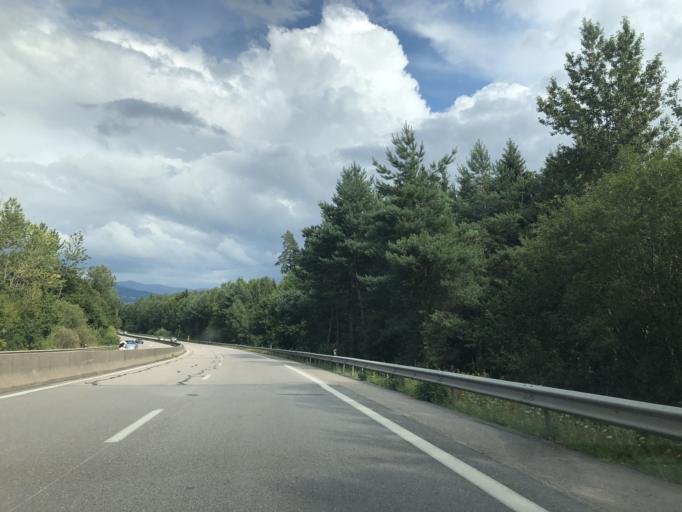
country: FR
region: Lorraine
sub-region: Departement des Vosges
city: Saint-Die-des-Vosges
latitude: 48.2629
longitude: 6.9495
